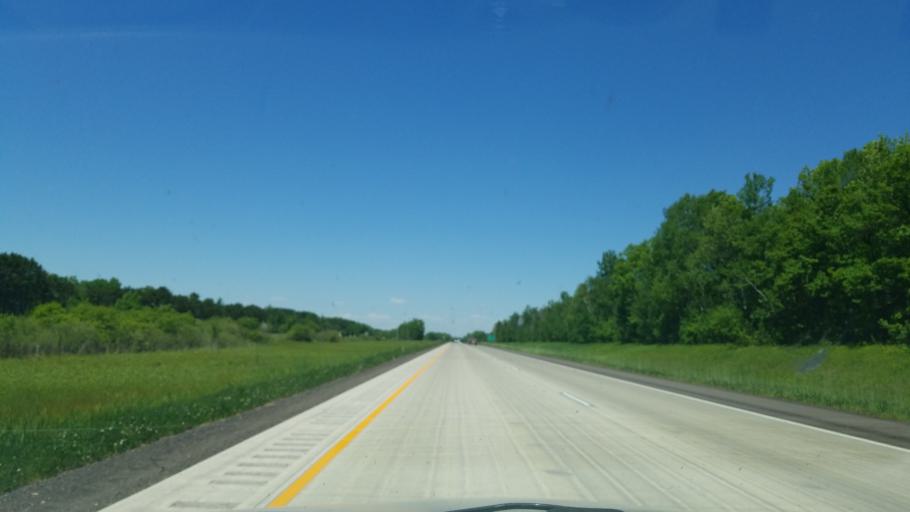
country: US
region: Minnesota
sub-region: Pine County
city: Pine City
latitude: 45.9141
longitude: -92.9666
